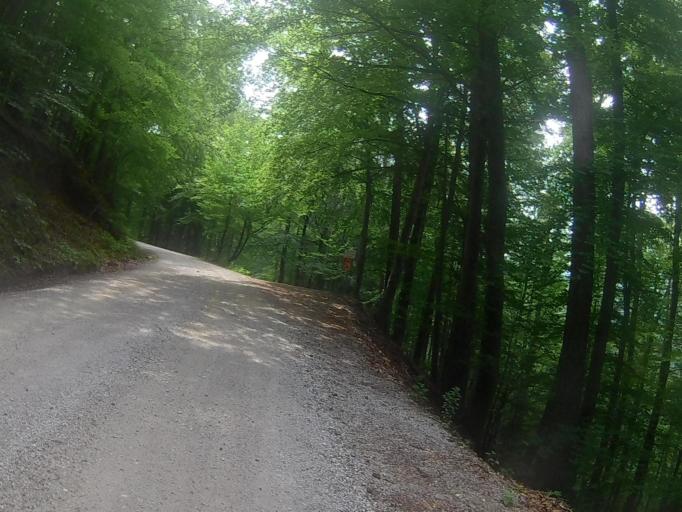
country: SI
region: Ruse
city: Ruse
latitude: 46.5258
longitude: 15.5362
